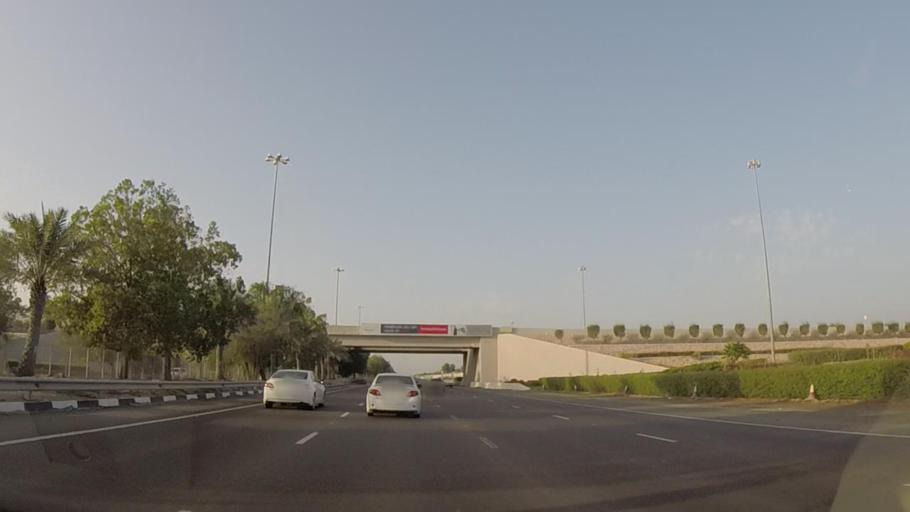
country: AE
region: Dubai
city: Dubai
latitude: 24.8609
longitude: 54.9070
